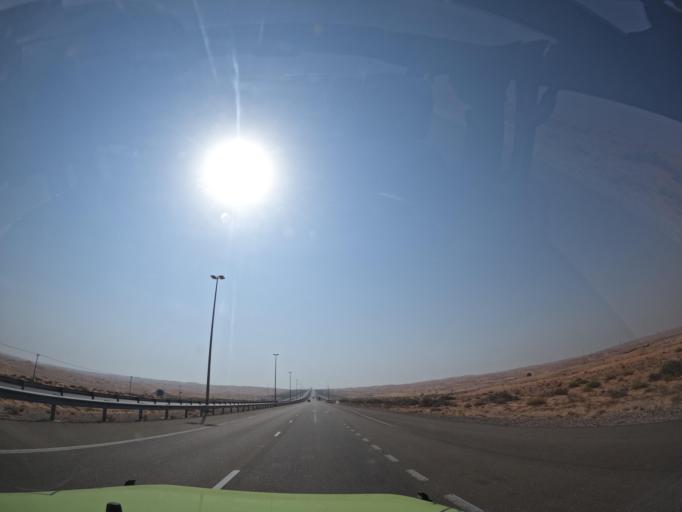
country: OM
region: Al Buraimi
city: Al Buraymi
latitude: 24.4421
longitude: 55.6631
